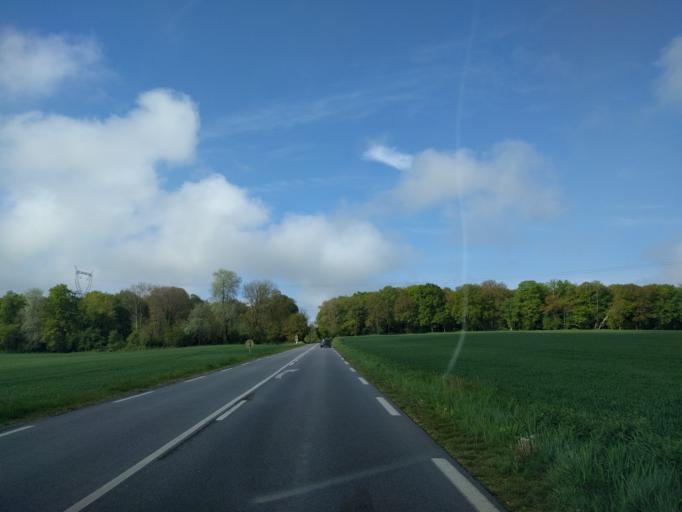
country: FR
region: Haute-Normandie
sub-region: Departement de l'Eure
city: Conches-en-Ouche
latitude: 48.9762
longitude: 1.0004
